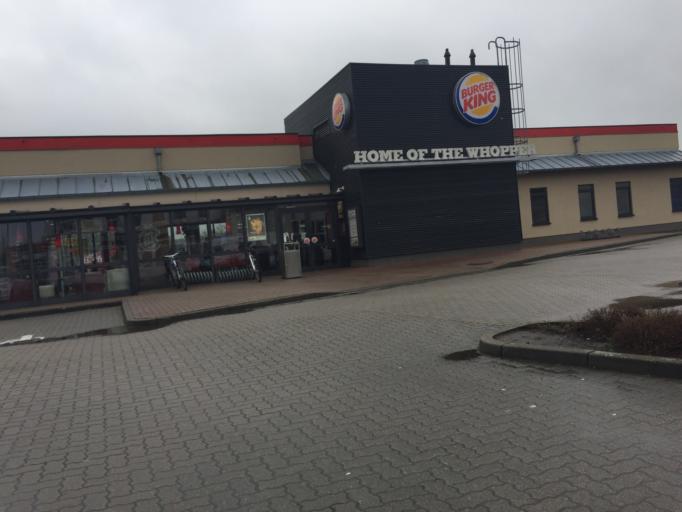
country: DE
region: Schleswig-Holstein
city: Itzehoe
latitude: 53.9154
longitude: 9.5152
